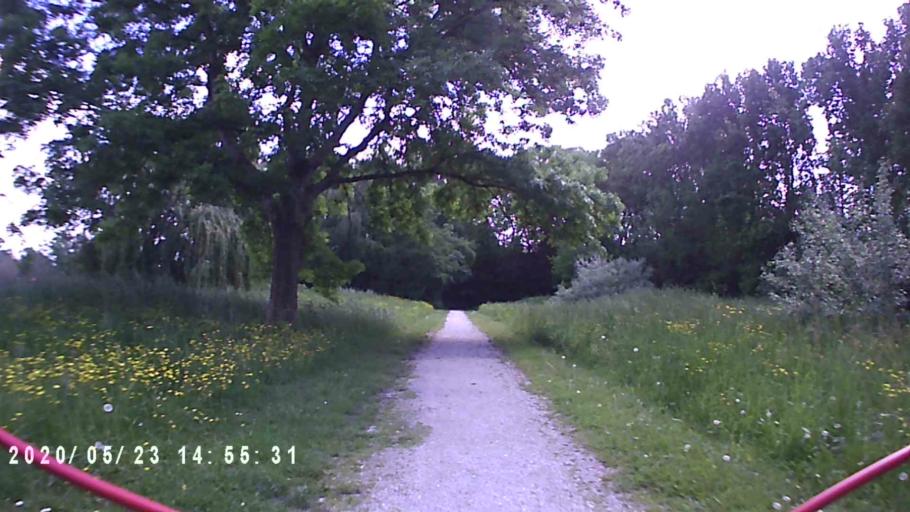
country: NL
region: Groningen
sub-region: Gemeente Delfzijl
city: Delfzijl
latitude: 53.2574
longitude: 6.9239
